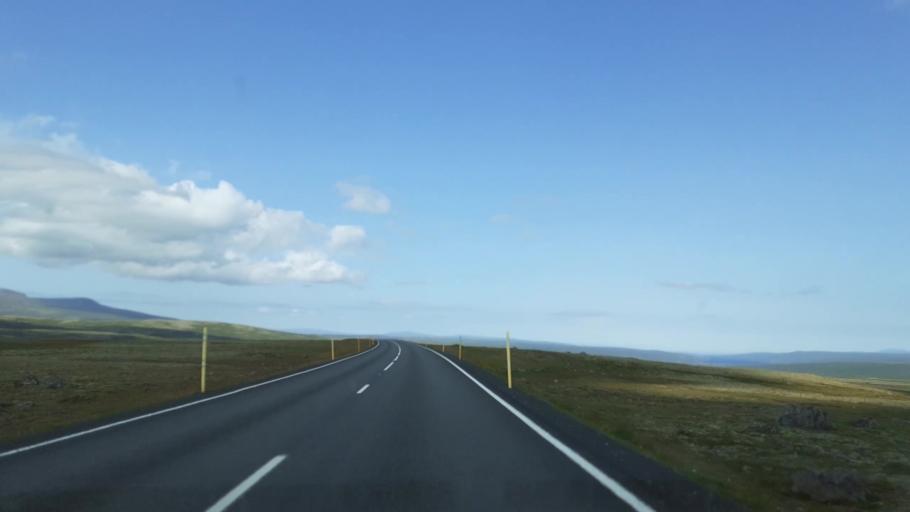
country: IS
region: West
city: Borgarnes
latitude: 65.0178
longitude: -21.0716
